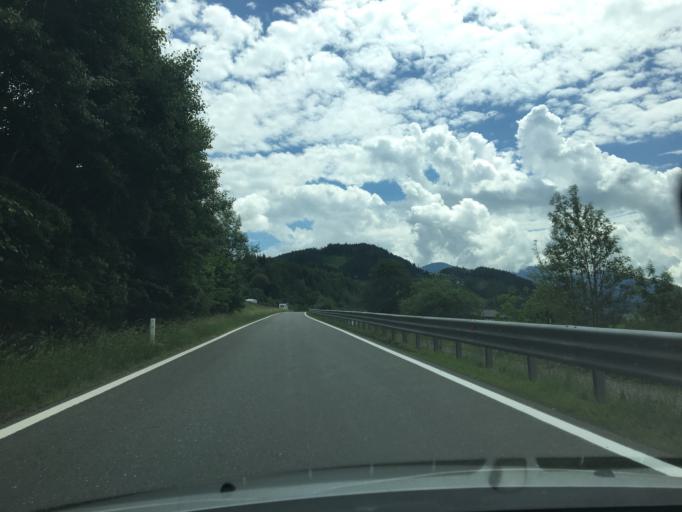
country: AT
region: Salzburg
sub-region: Politischer Bezirk Sankt Johann im Pongau
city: Pfarrwerfen
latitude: 47.4587
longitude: 13.2093
